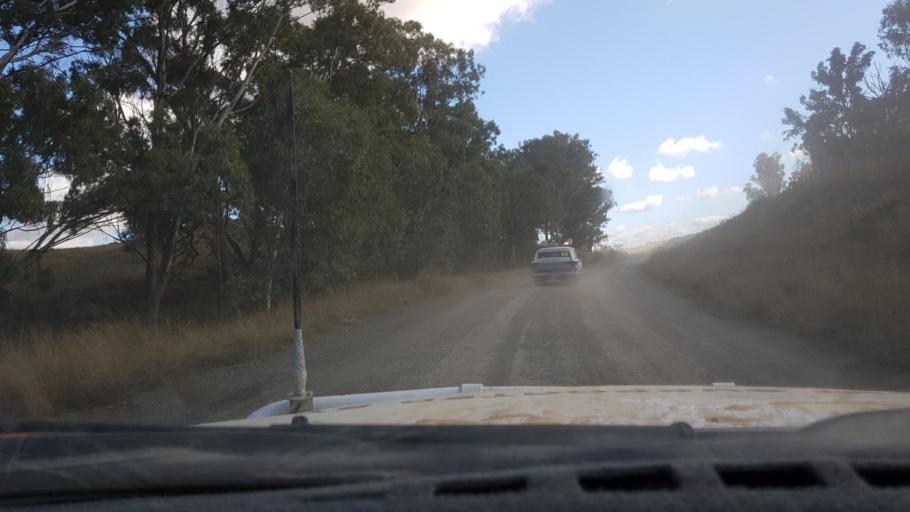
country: AU
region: New South Wales
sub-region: Tamworth Municipality
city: Manilla
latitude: -30.6092
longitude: 150.5054
